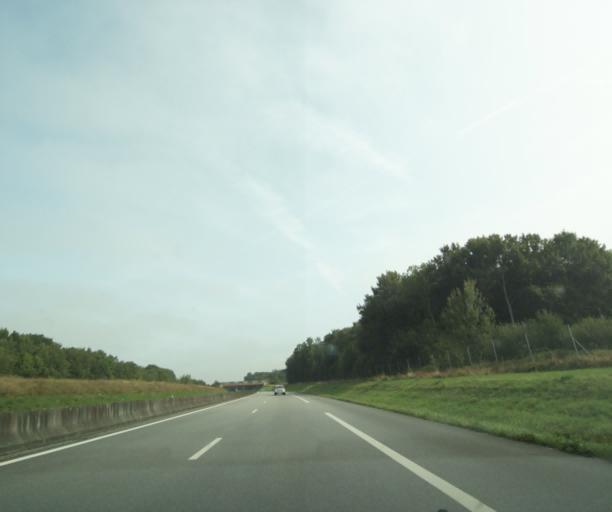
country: FR
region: Lower Normandy
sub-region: Departement de l'Orne
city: Sees
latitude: 48.5475
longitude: 0.1739
